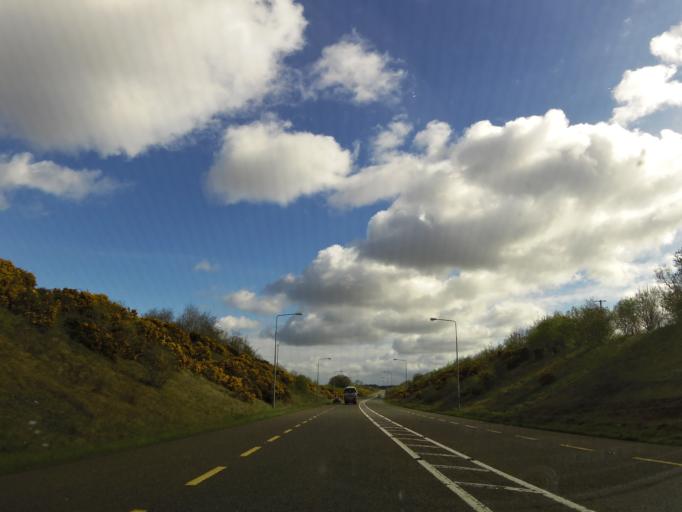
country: IE
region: Connaught
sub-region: Maigh Eo
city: Kiltamagh
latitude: 53.7978
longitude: -8.9234
